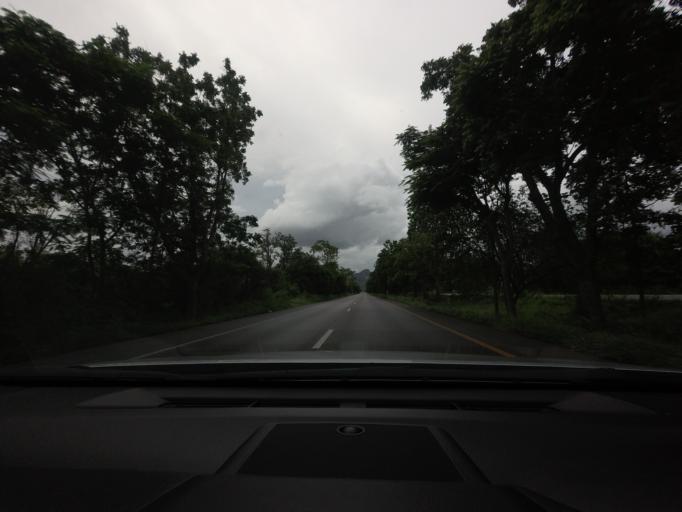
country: TH
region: Phetchaburi
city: Cha-am
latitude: 12.7843
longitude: 99.9383
